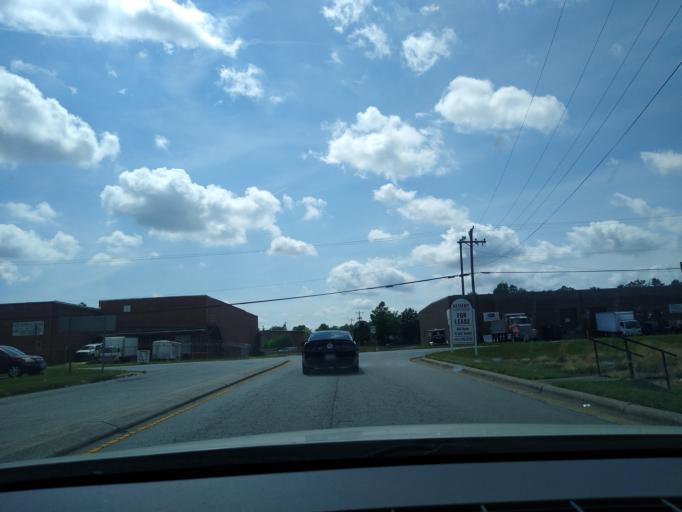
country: US
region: North Carolina
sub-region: Guilford County
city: Greensboro
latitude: 36.0861
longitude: -79.7651
